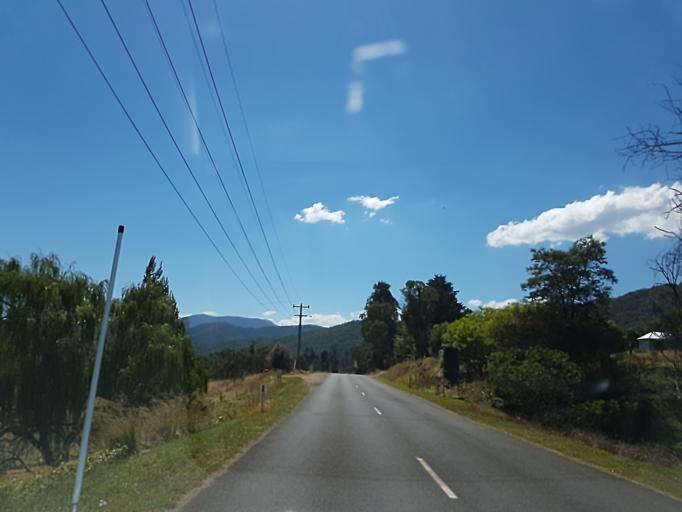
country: AU
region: Victoria
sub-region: Alpine
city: Mount Beauty
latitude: -36.7584
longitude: 146.9832
